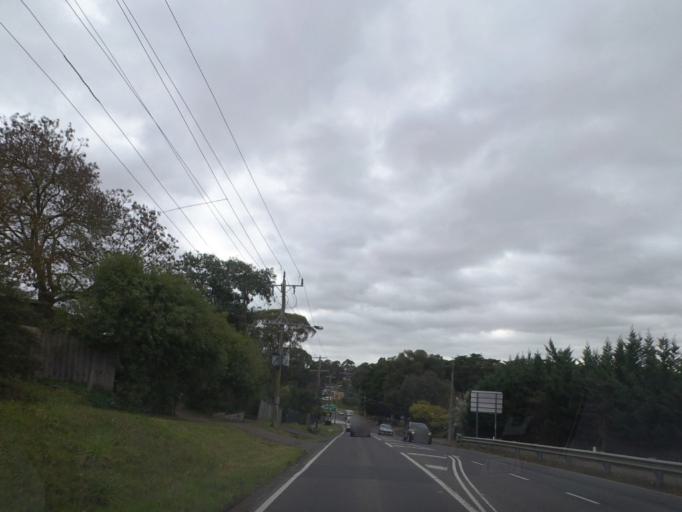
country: AU
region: Victoria
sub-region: Nillumbik
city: Diamond Creek
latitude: -37.6760
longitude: 145.1450
